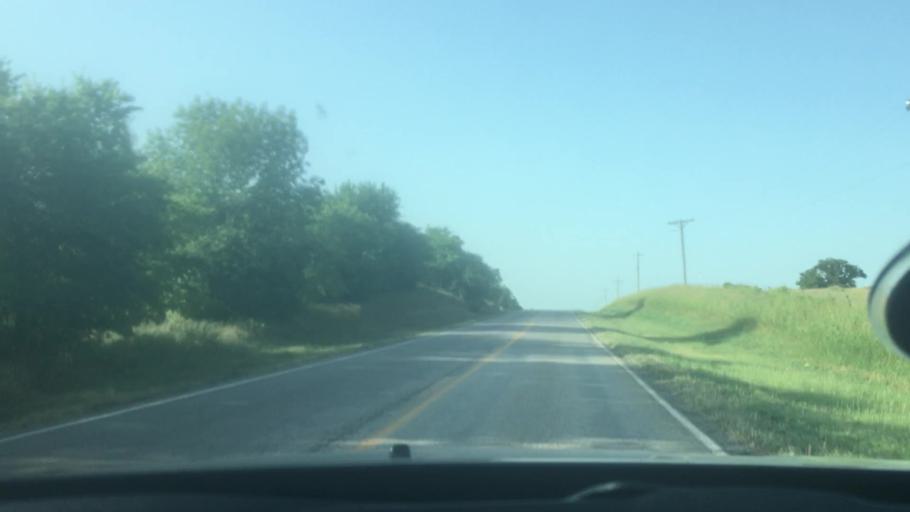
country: US
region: Oklahoma
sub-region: Coal County
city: Coalgate
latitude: 34.4133
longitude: -96.4246
